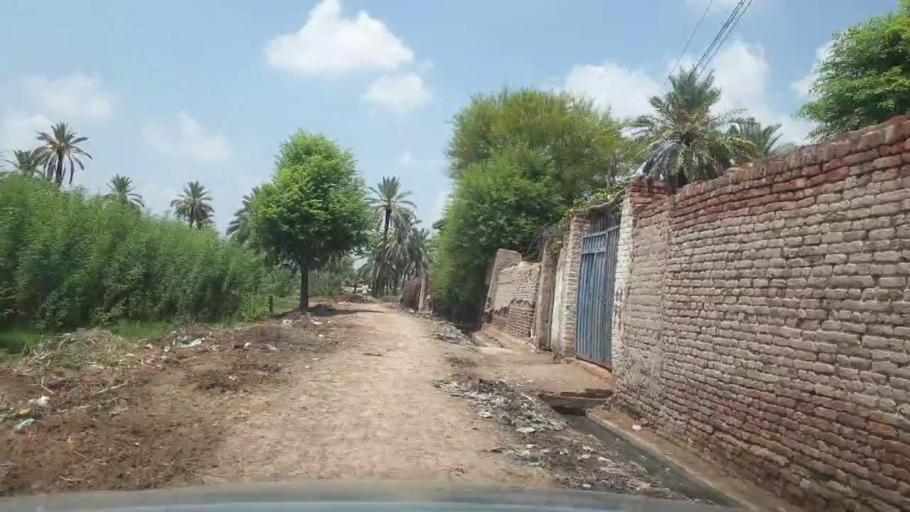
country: PK
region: Sindh
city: Pir jo Goth
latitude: 27.6121
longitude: 68.6041
